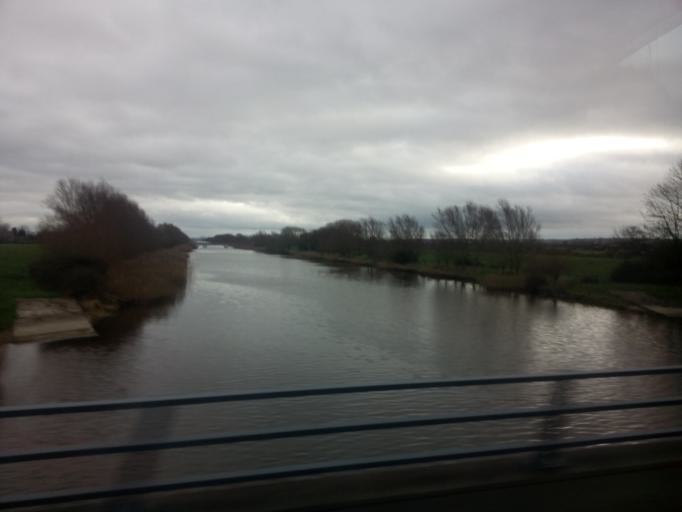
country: GB
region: England
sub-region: Somerset
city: Puriton
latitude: 51.1942
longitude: -2.9707
